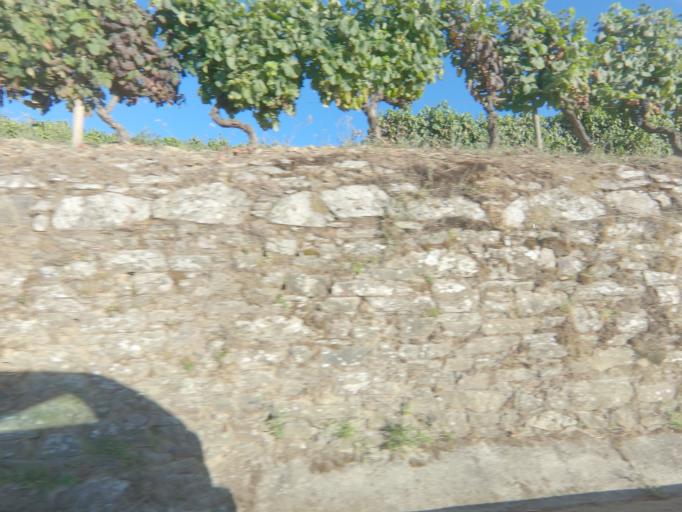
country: PT
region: Vila Real
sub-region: Peso da Regua
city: Godim
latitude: 41.1654
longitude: -7.8302
